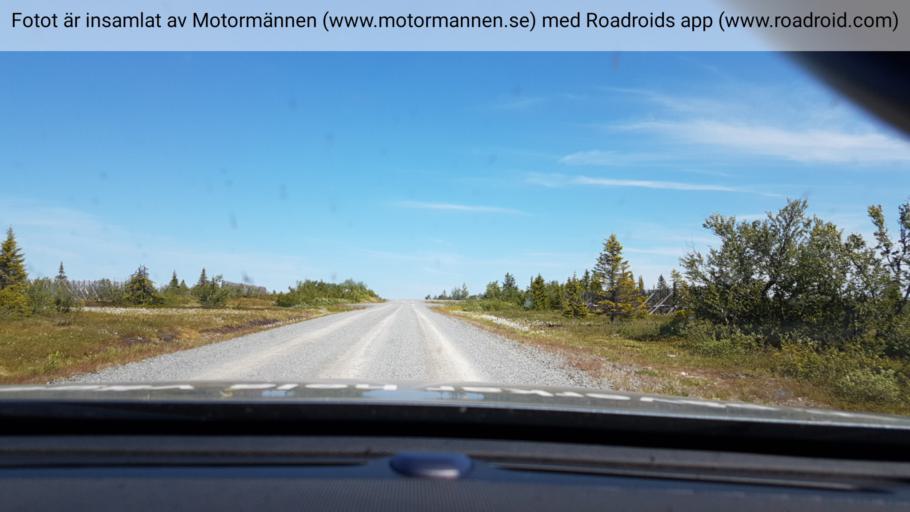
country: SE
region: Vaesterbotten
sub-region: Vilhelmina Kommun
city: Sjoberg
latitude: 64.7487
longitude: 15.8189
